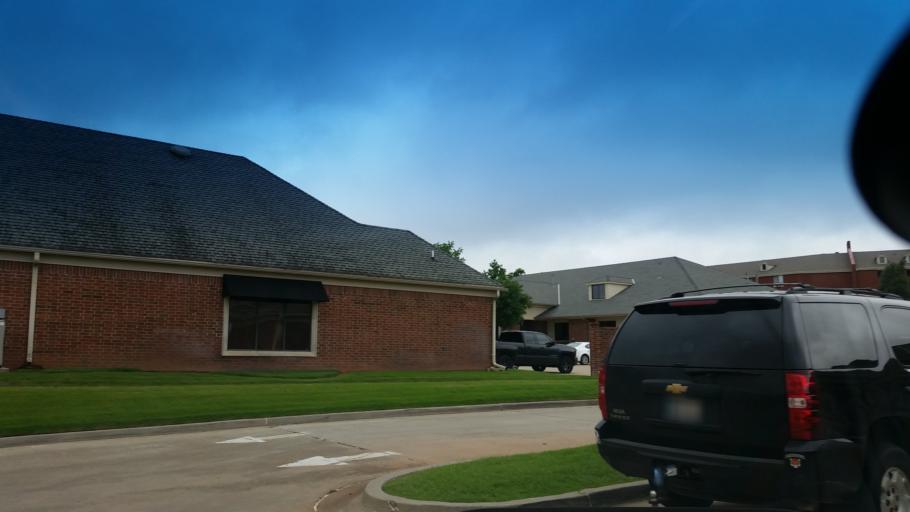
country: US
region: Oklahoma
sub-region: Oklahoma County
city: Edmond
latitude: 35.6583
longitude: -97.4609
